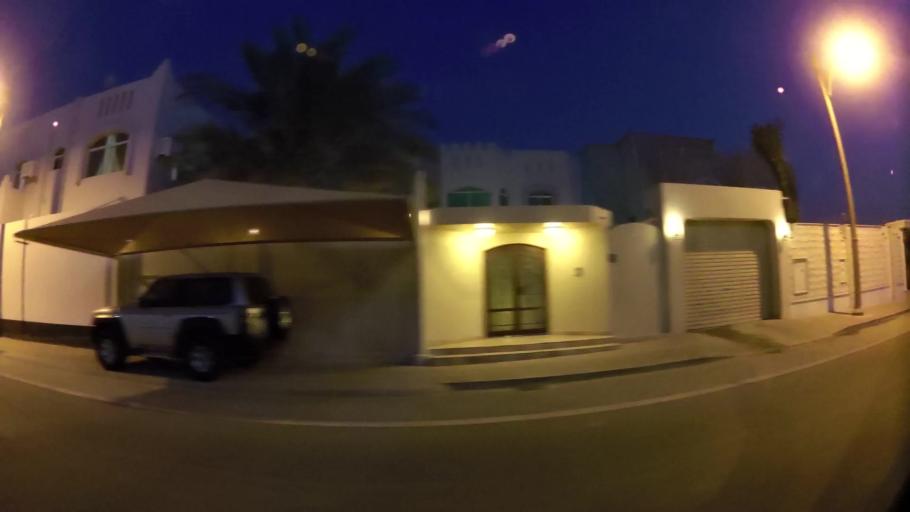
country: QA
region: Baladiyat ad Dawhah
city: Doha
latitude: 25.2570
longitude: 51.4801
